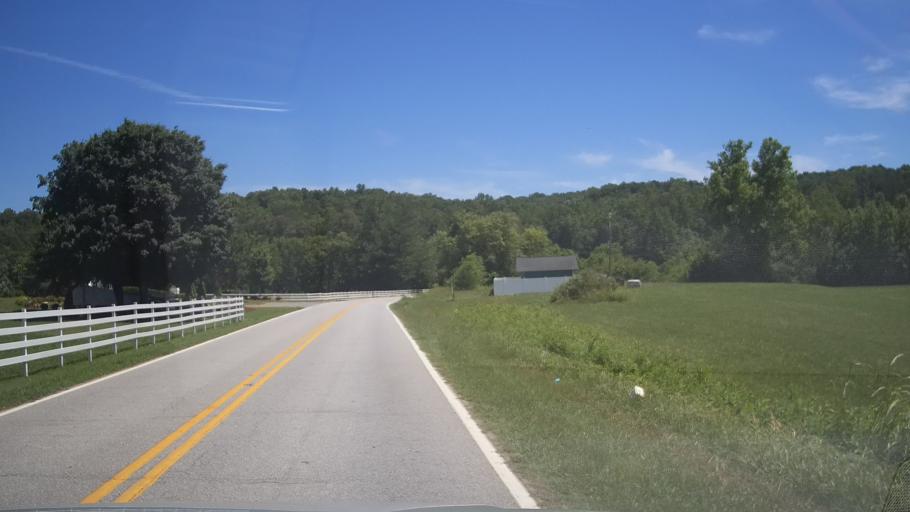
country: US
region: North Carolina
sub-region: Rutherford County
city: Rutherfordton
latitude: 35.2972
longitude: -81.9850
